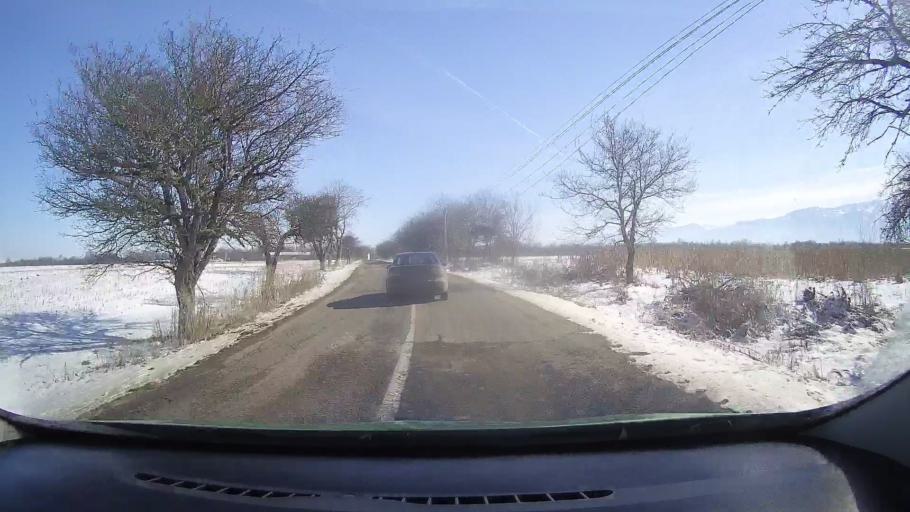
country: RO
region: Brasov
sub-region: Comuna Recea
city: Recea
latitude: 45.7327
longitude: 24.9279
